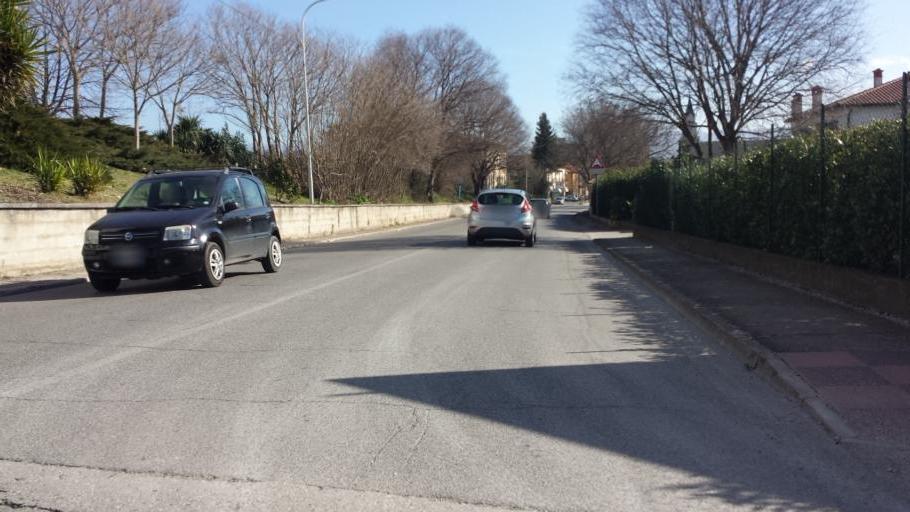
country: IT
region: Umbria
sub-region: Provincia di Terni
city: Terni
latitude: 42.5850
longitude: 12.6124
